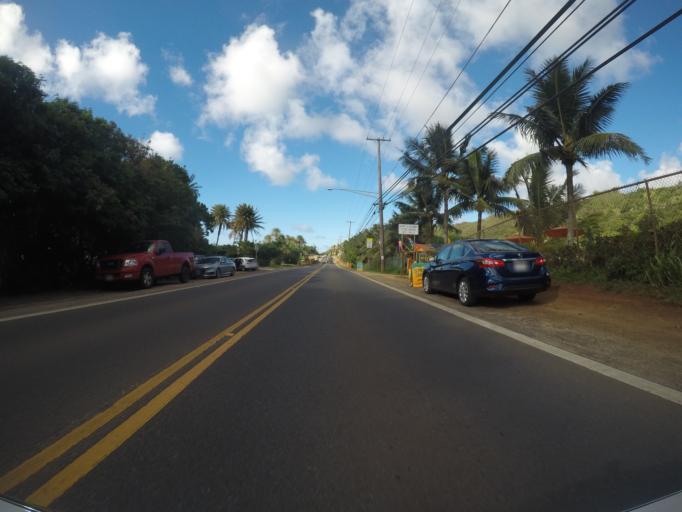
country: US
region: Hawaii
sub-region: Honolulu County
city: Pupukea
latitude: 21.6720
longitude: -158.0423
